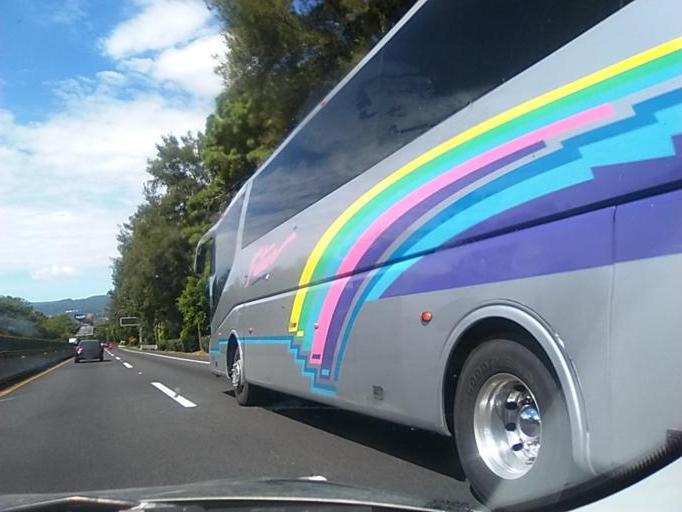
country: MX
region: Morelos
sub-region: Cuernavaca
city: Lomas de Ahuatepec
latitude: 18.9822
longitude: -99.2192
